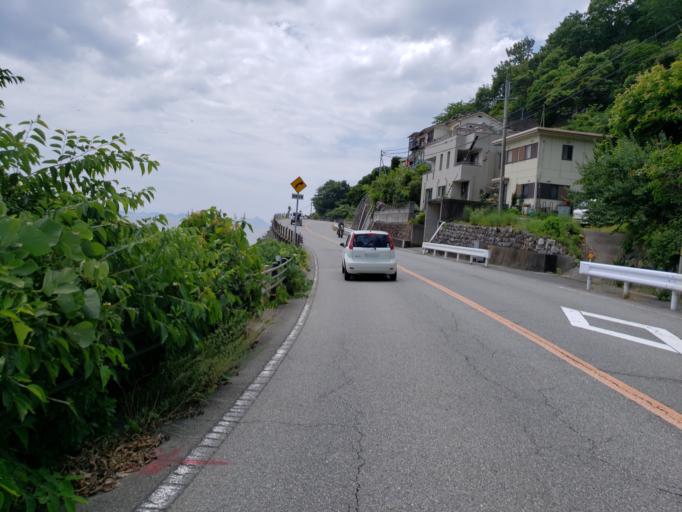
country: JP
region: Hyogo
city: Aioi
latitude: 34.7832
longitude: 134.5269
